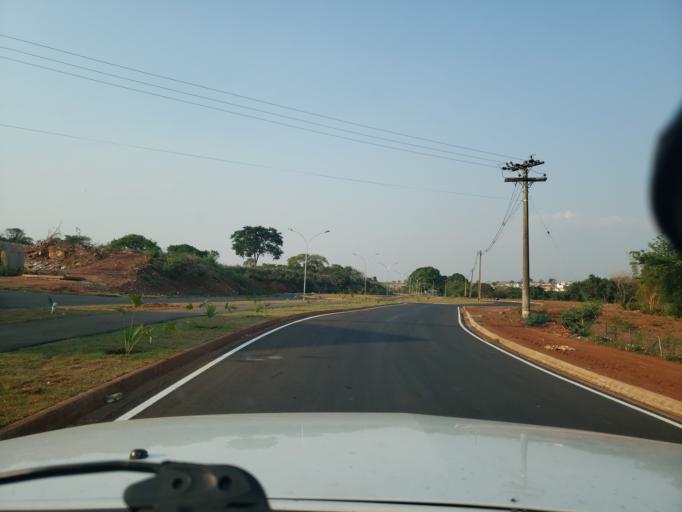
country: BR
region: Sao Paulo
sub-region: Moji-Guacu
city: Mogi-Gaucu
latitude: -22.3261
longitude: -46.9503
